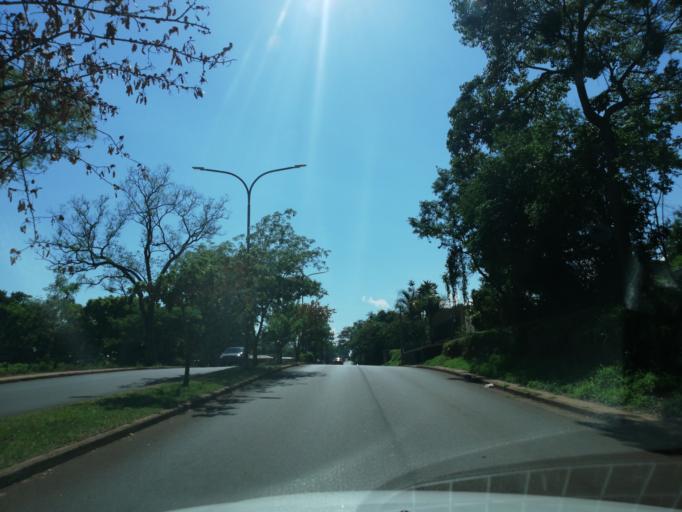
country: AR
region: Misiones
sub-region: Departamento de Capital
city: Posadas
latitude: -27.3644
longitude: -55.9416
